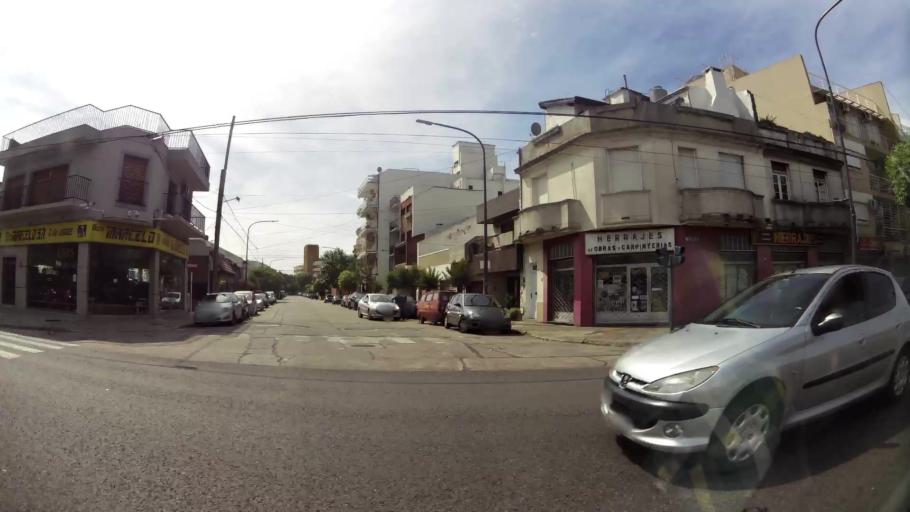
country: AR
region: Buenos Aires F.D.
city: Villa Lugano
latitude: -34.6506
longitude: -58.5126
